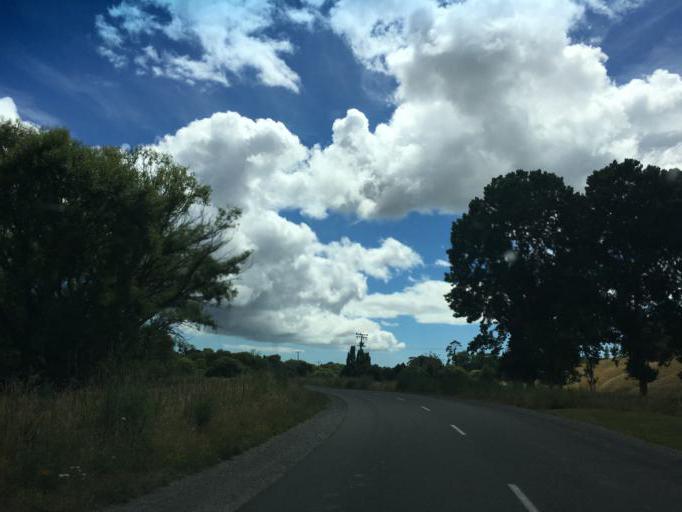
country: NZ
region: Hawke's Bay
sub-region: Hastings District
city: Hastings
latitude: -39.7519
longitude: 176.8745
